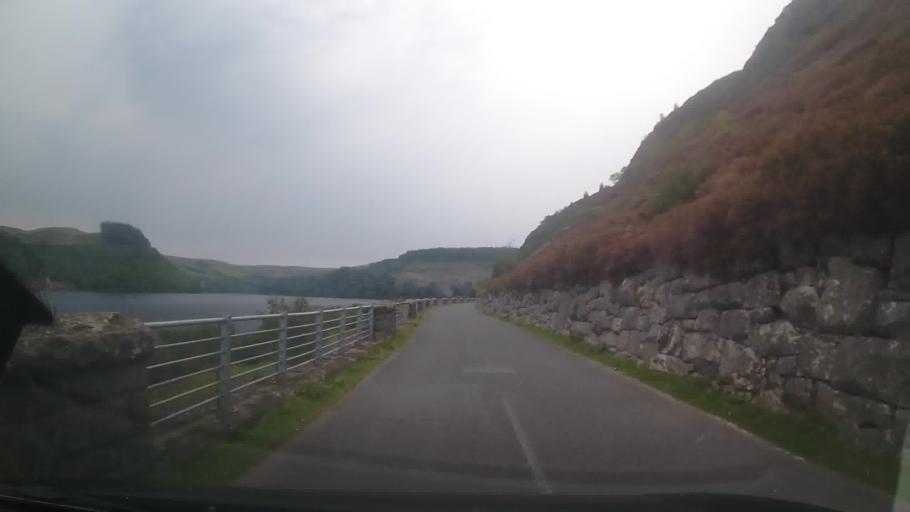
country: GB
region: Wales
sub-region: Sir Powys
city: Rhayader
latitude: 52.2675
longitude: -3.5822
